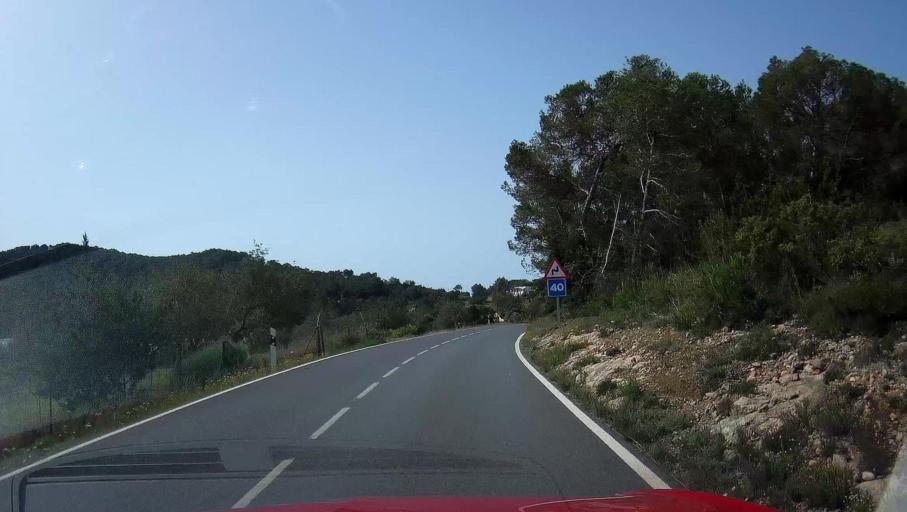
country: ES
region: Balearic Islands
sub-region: Illes Balears
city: Sant Joan de Labritja
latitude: 39.0437
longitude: 1.5674
